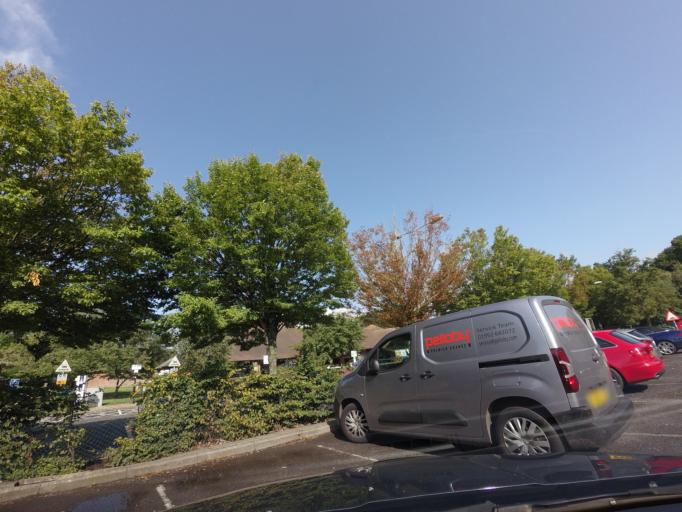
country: GB
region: England
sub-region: Kent
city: Harrietsham
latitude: 51.2668
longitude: 0.6147
